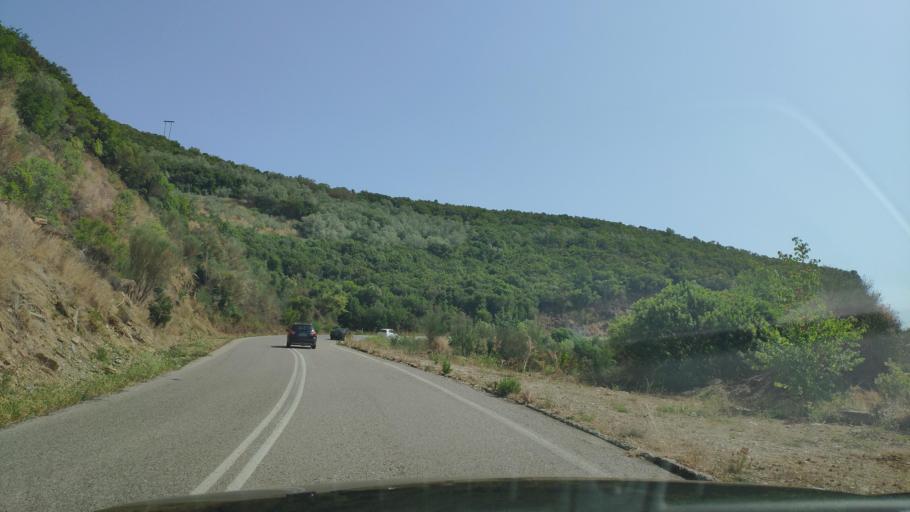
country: GR
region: Epirus
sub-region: Nomos Artas
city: Peta
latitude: 39.1686
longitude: 21.0667
